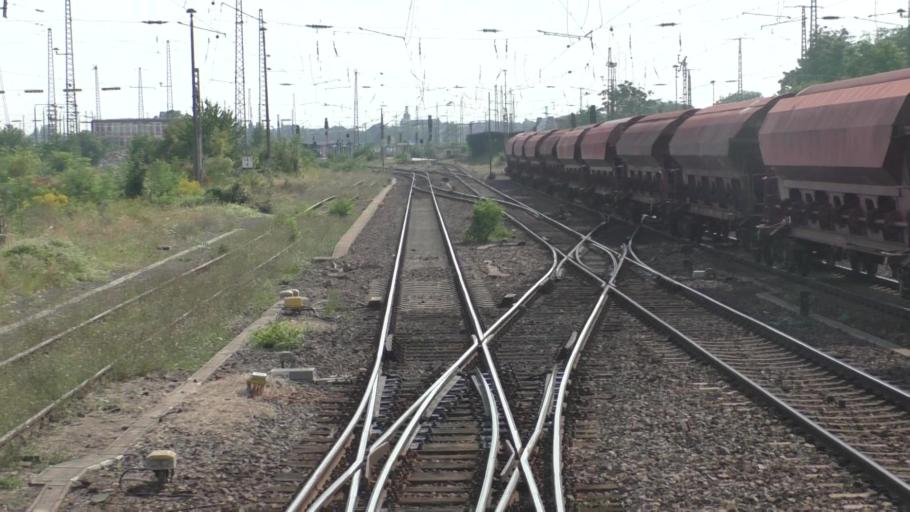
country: DE
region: Saxony-Anhalt
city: Magdeburg
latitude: 52.1358
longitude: 11.6283
